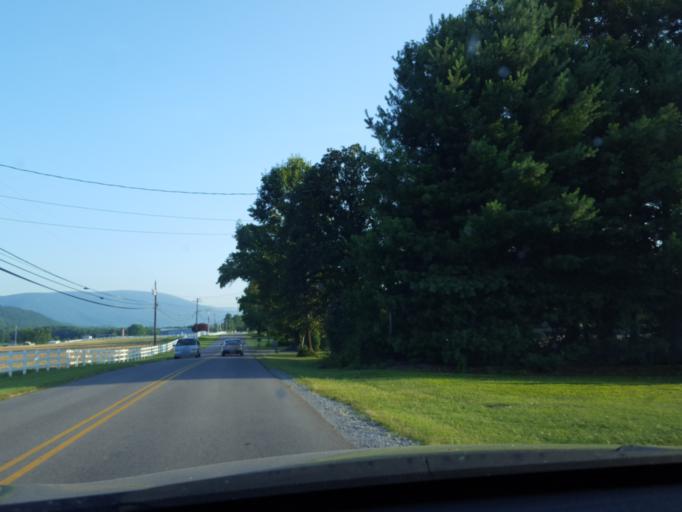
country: US
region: Virginia
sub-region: Augusta County
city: Lyndhurst
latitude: 38.0203
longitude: -78.9467
